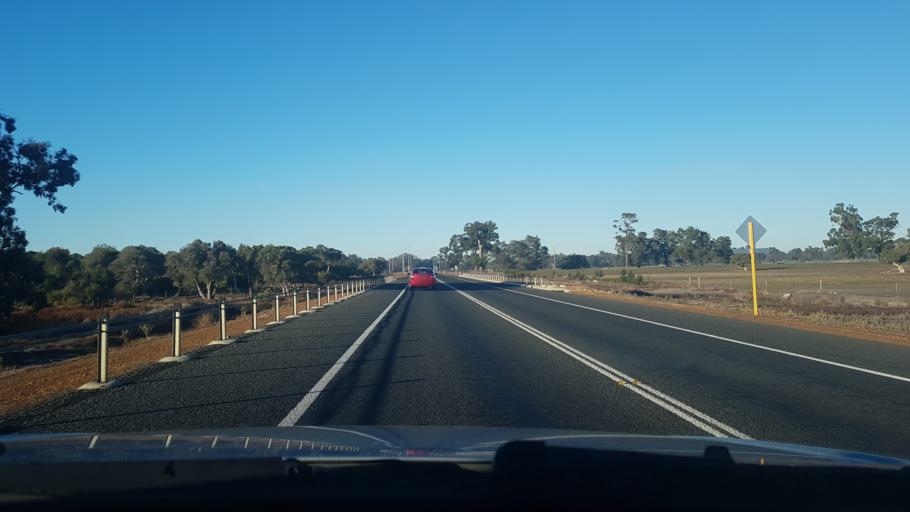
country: AU
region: Western Australia
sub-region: Busselton
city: Vasse
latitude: -33.6800
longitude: 115.2302
